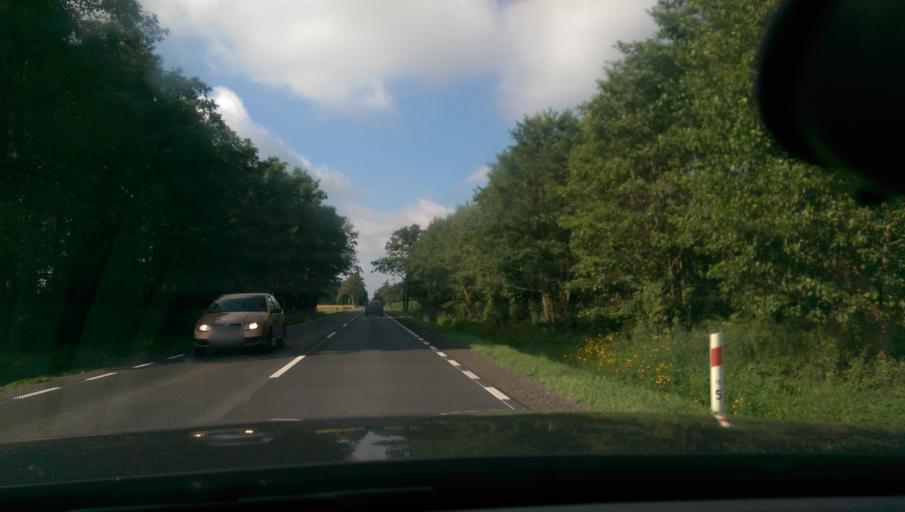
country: PL
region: Masovian Voivodeship
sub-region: Powiat ciechanowski
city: Ojrzen
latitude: 52.7318
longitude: 20.5152
